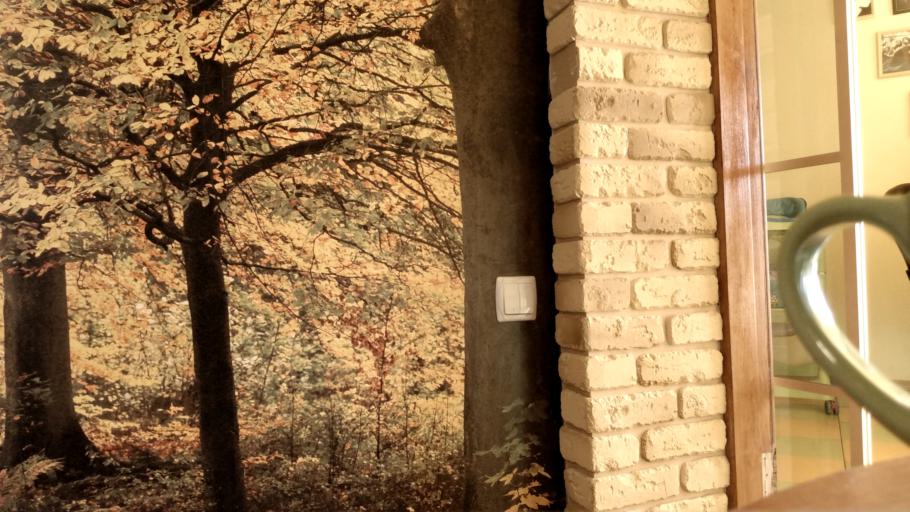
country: RU
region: Vologda
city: Imeni Zhelyabova
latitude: 58.8666
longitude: 36.8411
